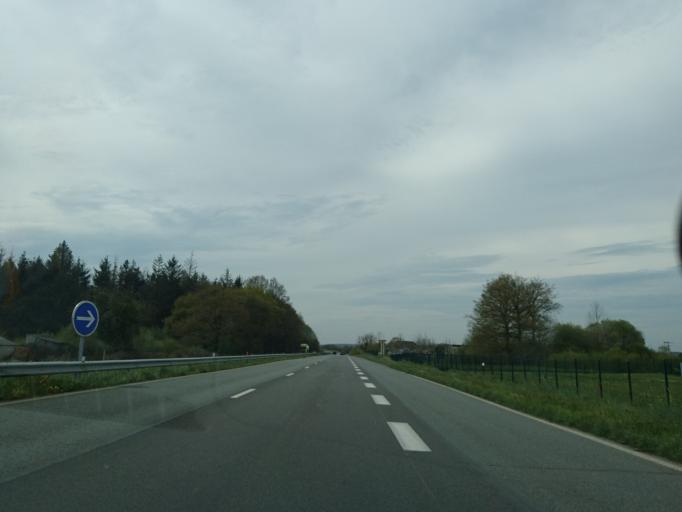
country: FR
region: Brittany
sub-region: Departement des Cotes-d'Armor
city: Jugon-les-Lacs
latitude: 48.4092
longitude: -2.3487
